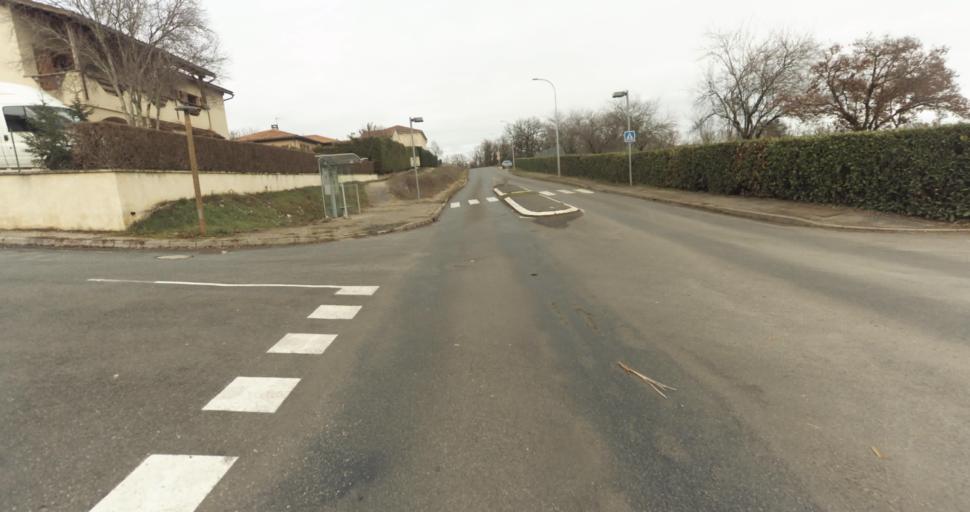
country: FR
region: Midi-Pyrenees
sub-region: Departement du Lot
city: Figeac
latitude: 44.6092
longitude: 2.0107
